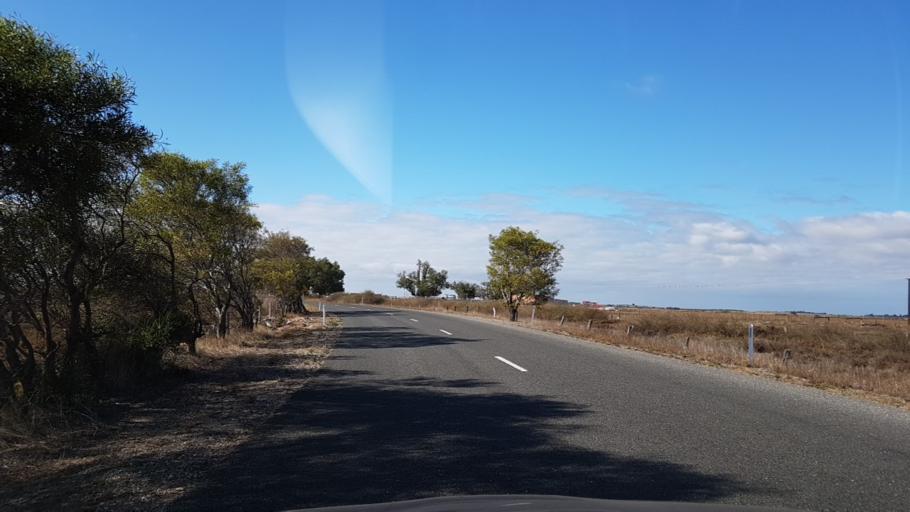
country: AU
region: South Australia
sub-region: Alexandrina
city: Goolwa
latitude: -35.4544
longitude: 138.9500
